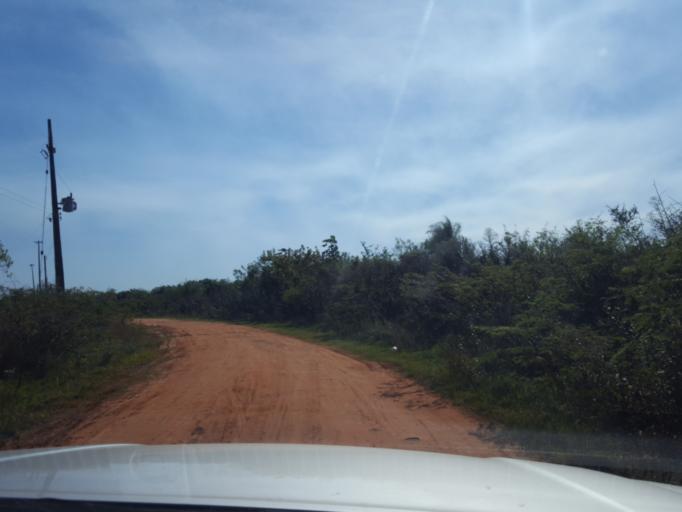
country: PY
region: Cordillera
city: Atyra
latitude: -25.2461
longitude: -57.1267
